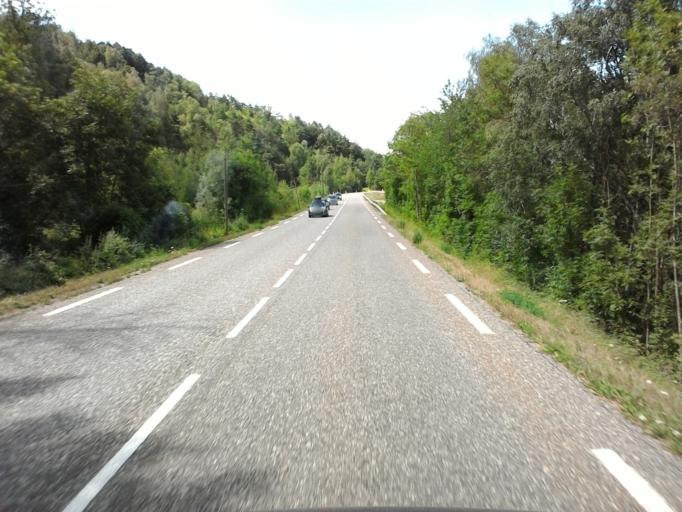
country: FR
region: Provence-Alpes-Cote d'Azur
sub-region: Departement des Hautes-Alpes
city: Saint-Bonnet-en-Champsaur
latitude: 44.6934
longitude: 6.0612
